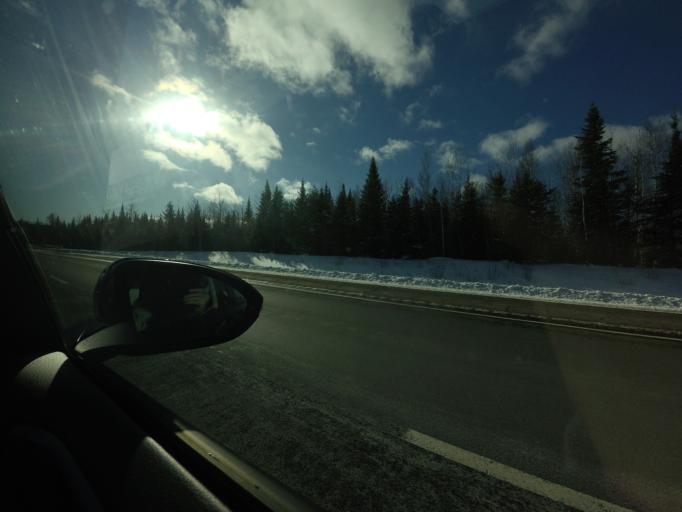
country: CA
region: New Brunswick
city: Fredericton
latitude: 45.8782
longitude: -66.6344
